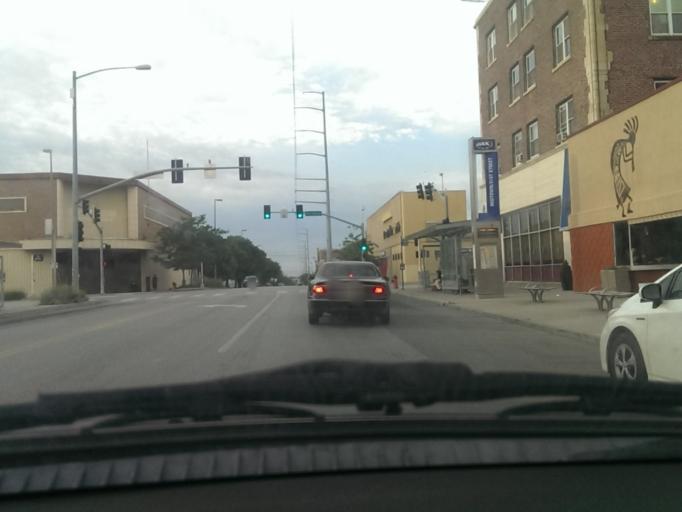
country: US
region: Missouri
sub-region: Jackson County
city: Kansas City
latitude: 39.0700
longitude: -94.5713
